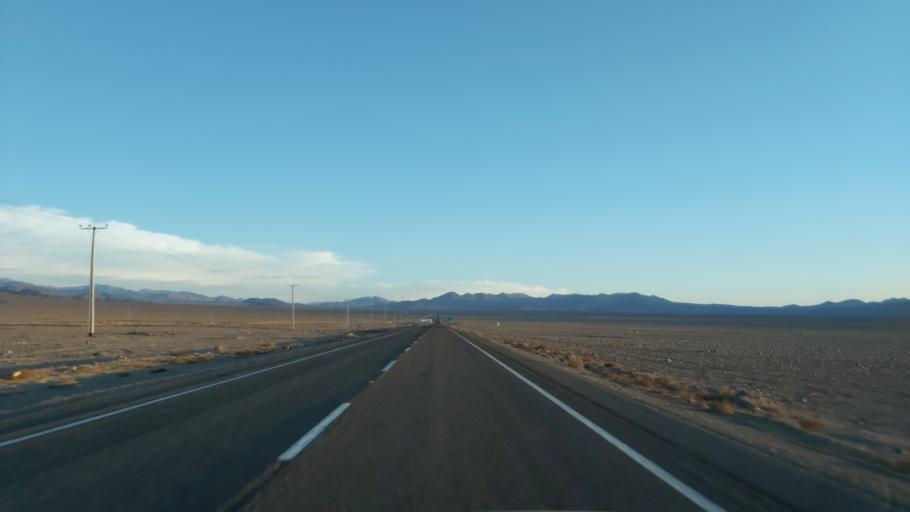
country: CL
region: Atacama
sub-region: Provincia de Chanaral
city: Diego de Almagro
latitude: -26.6241
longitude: -69.9510
